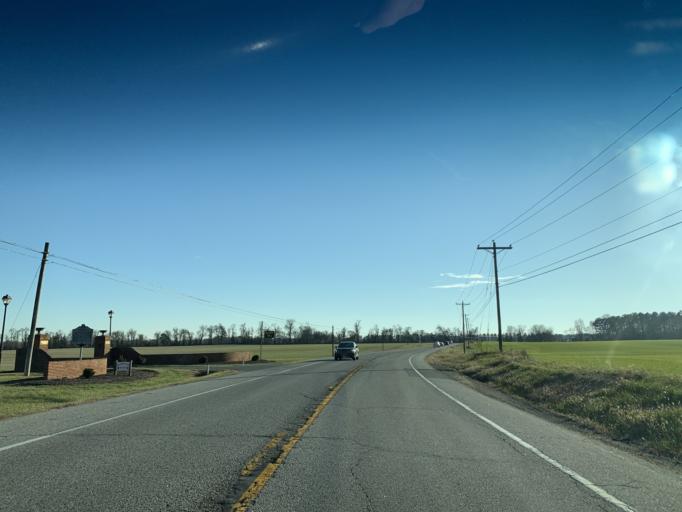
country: US
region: Delaware
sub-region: New Castle County
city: Middletown
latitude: 39.3901
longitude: -75.8713
